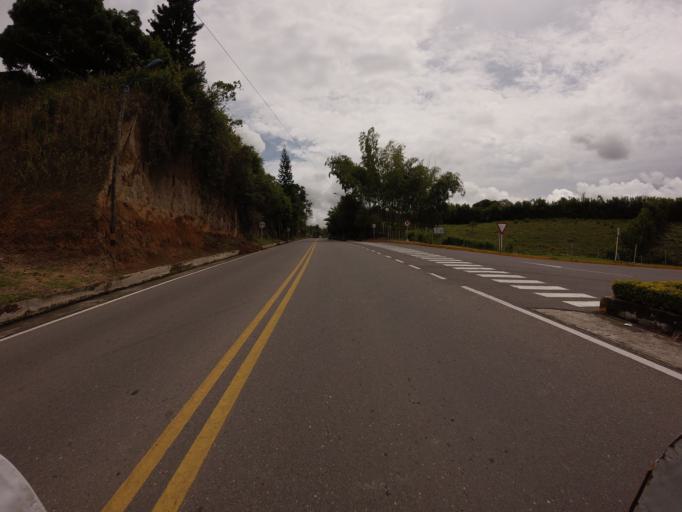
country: CO
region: Valle del Cauca
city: Alcala
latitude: 4.6658
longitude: -75.7806
